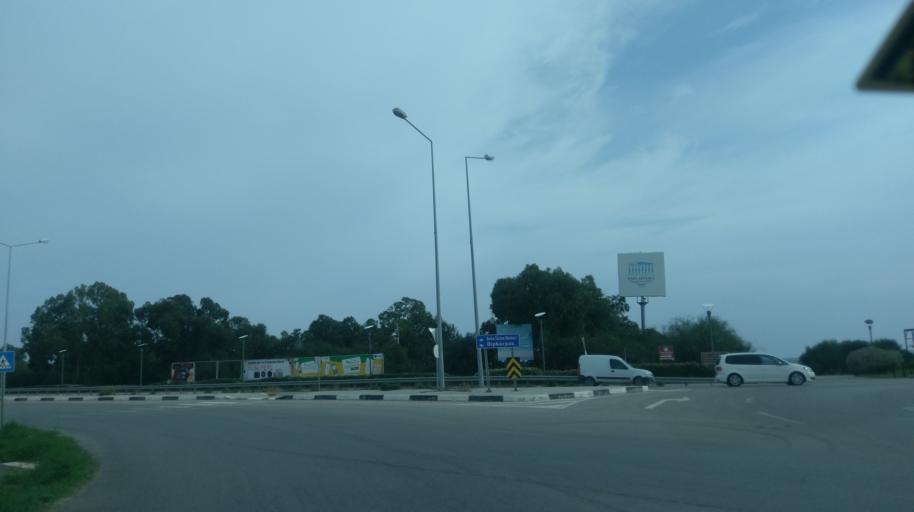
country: CY
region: Ammochostos
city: Trikomo
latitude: 35.2789
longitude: 33.9201
